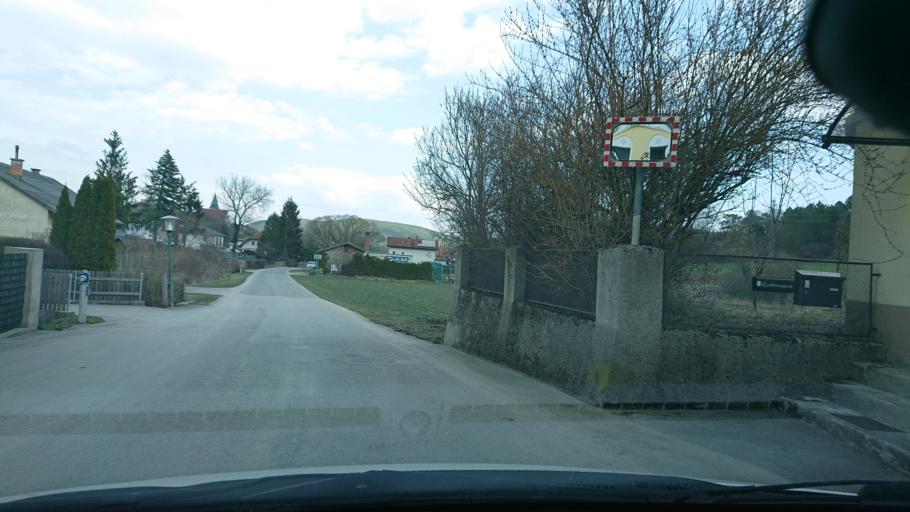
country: AT
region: Lower Austria
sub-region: Politischer Bezirk Baden
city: Berndorf
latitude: 47.9242
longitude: 16.0797
